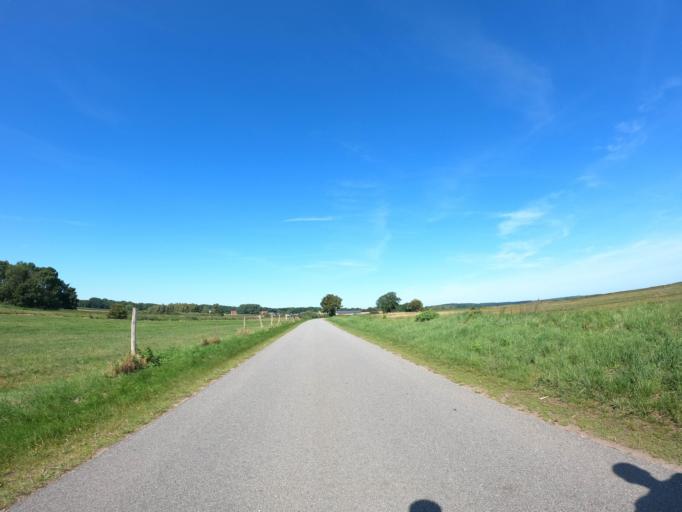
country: DE
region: Mecklenburg-Vorpommern
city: Prohn
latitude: 54.3959
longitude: 13.0226
